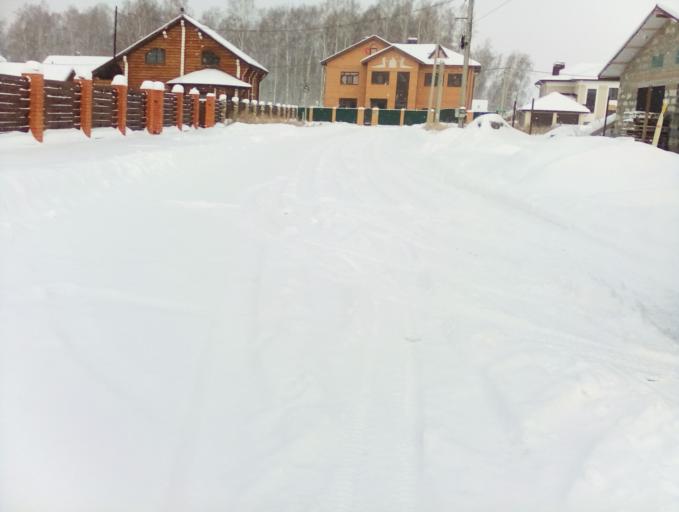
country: RU
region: Chelyabinsk
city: Poletayevo
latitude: 55.1546
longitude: 61.1400
